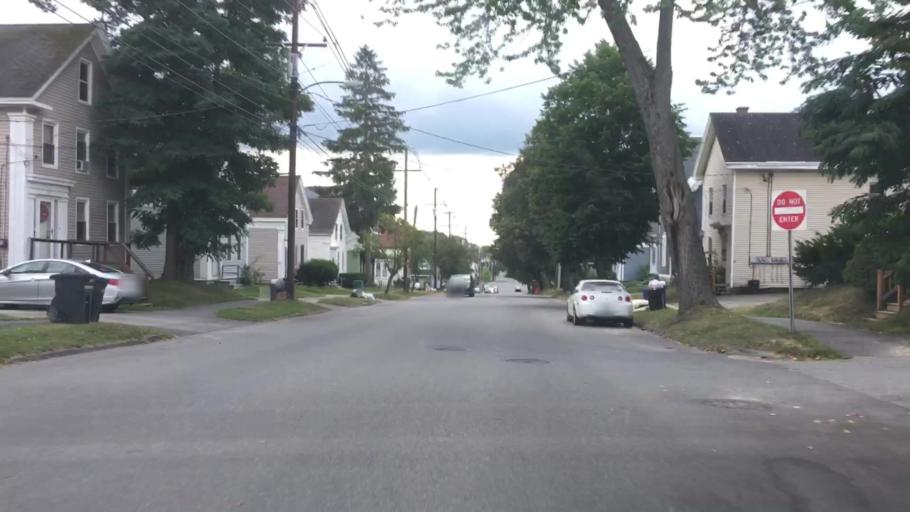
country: US
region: Maine
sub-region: Penobscot County
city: Bangor
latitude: 44.8119
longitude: -68.7727
